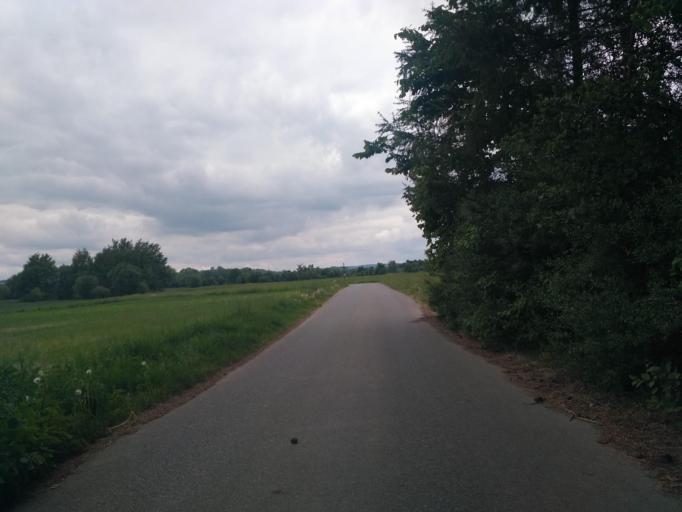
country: PL
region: Subcarpathian Voivodeship
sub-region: Powiat krosnienski
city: Jedlicze
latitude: 49.7040
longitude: 21.6761
